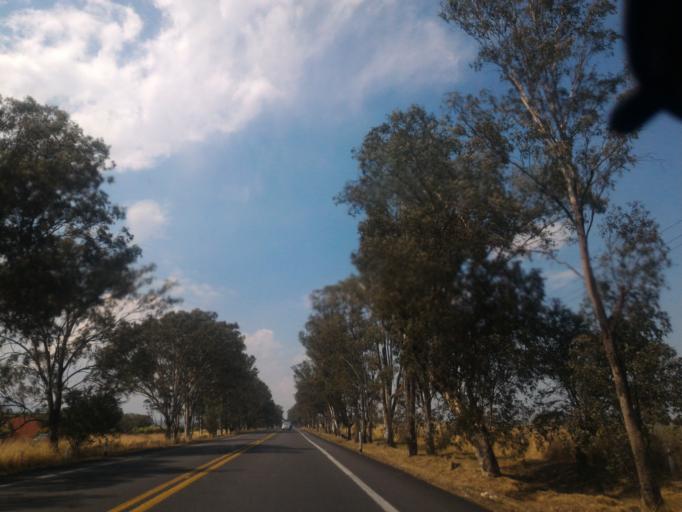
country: MX
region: Jalisco
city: Tuxpan
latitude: 19.5483
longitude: -103.4323
